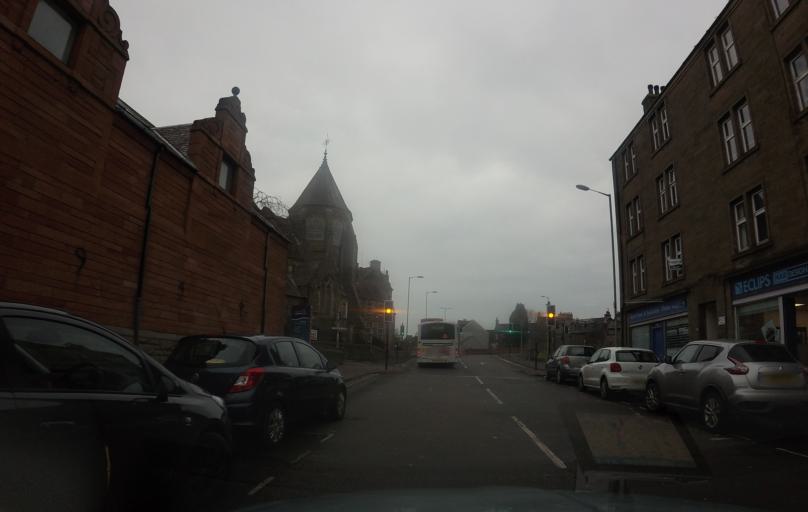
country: GB
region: Scotland
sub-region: Dundee City
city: Dundee
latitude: 56.4708
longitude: -3.0086
